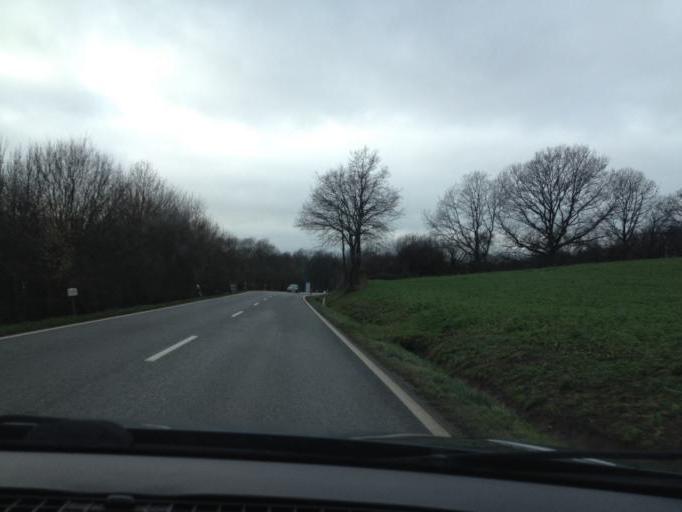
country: DE
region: Saarland
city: Sankt Wendel
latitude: 49.4550
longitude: 7.1888
